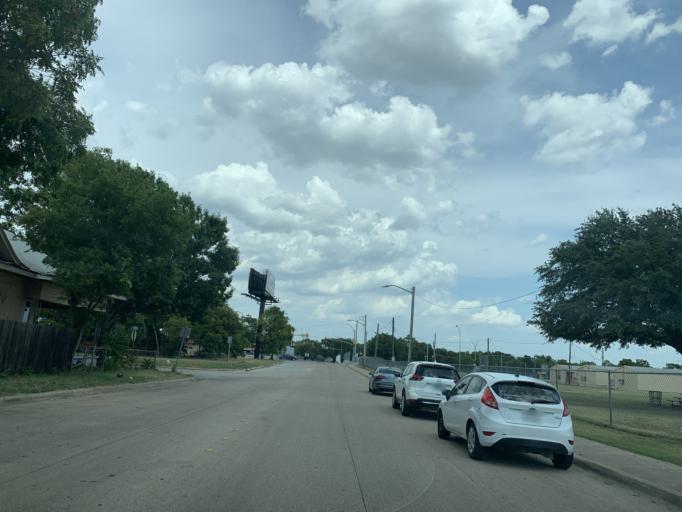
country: US
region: Texas
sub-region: Tarrant County
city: Fort Worth
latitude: 32.6970
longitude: -97.3225
